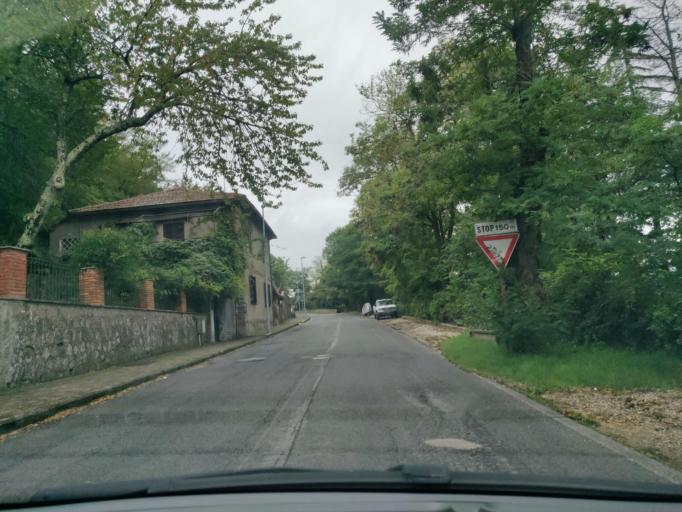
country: IT
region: Latium
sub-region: Citta metropolitana di Roma Capitale
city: Allumiere
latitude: 42.1538
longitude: 11.9035
